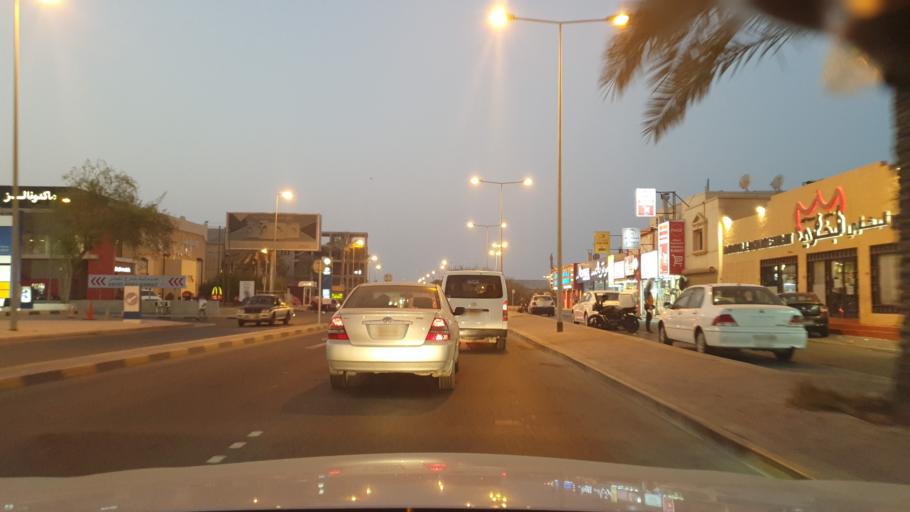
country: BH
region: Muharraq
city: Al Muharraq
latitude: 26.2664
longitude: 50.6158
